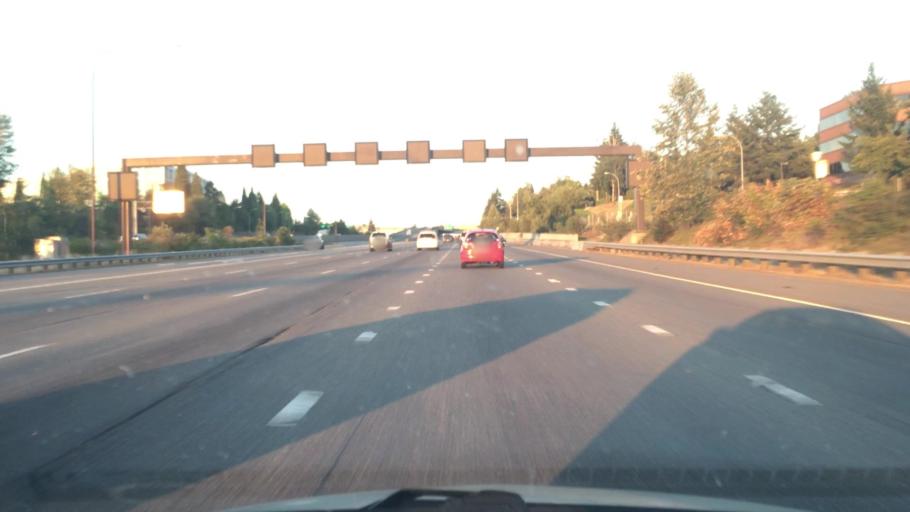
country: US
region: Washington
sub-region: King County
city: Eastgate
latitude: 47.5794
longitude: -122.1609
